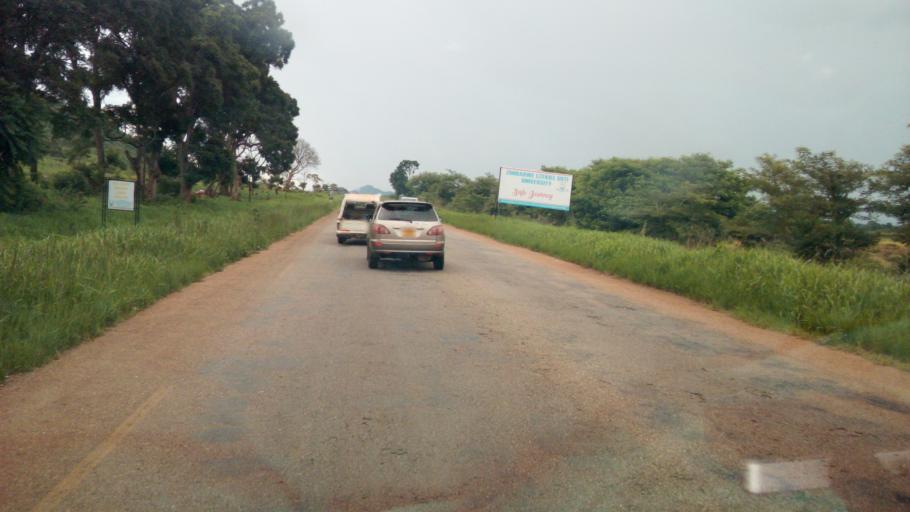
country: ZW
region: Mashonaland Central
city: Bindura
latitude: -17.3054
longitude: 31.2894
